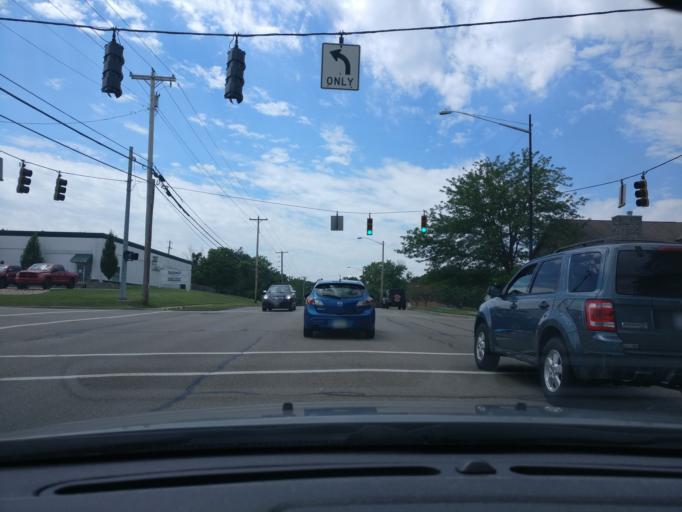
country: US
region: Ohio
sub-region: Montgomery County
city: West Carrollton City
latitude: 39.6542
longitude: -84.2424
